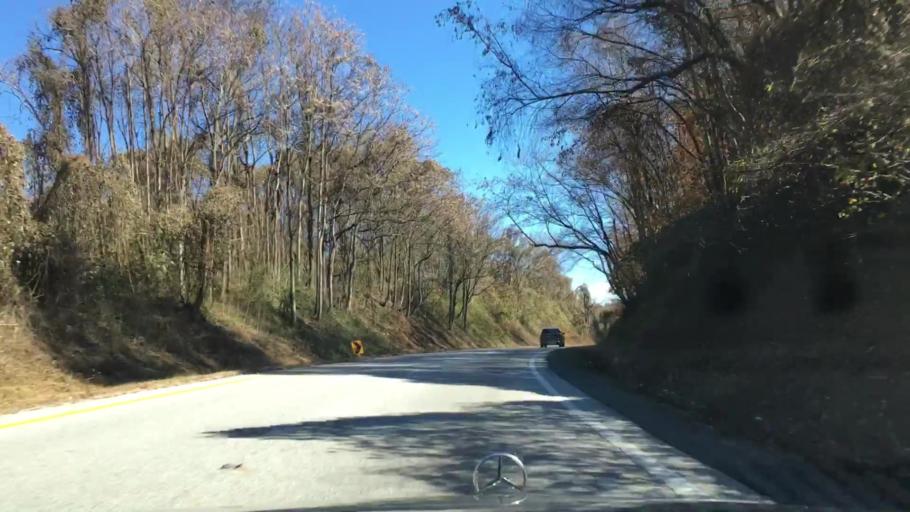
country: US
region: Virginia
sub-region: Nelson County
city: Nellysford
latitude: 37.8437
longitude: -78.7901
